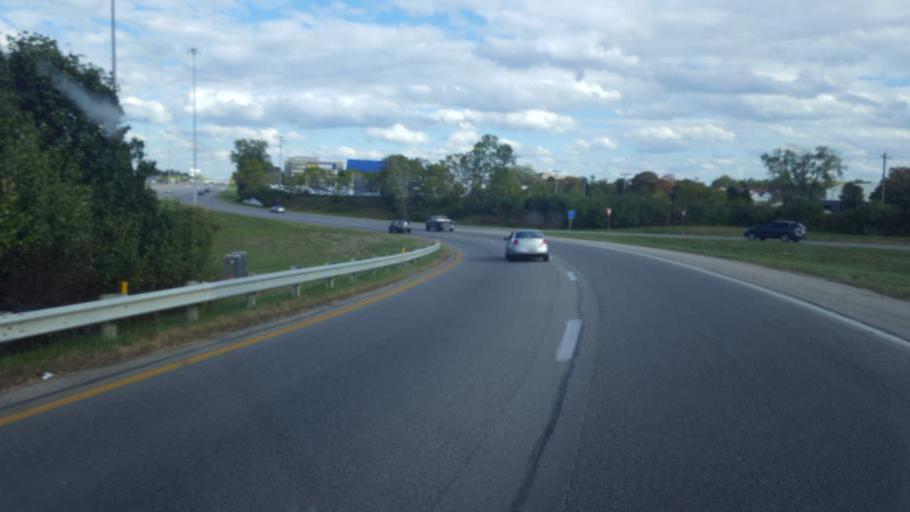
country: US
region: Ohio
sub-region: Franklin County
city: Dublin
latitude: 40.1084
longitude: -83.0904
